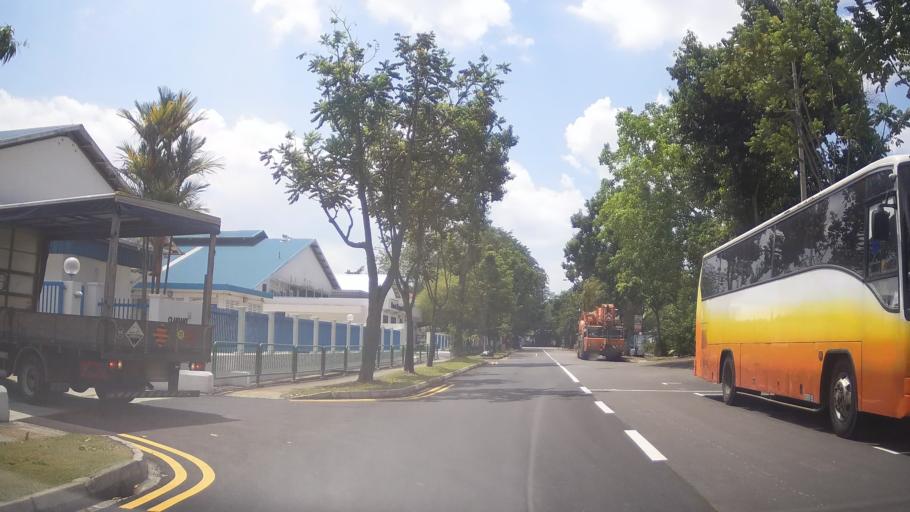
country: MY
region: Johor
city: Johor Bahru
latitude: 1.3327
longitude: 103.7160
